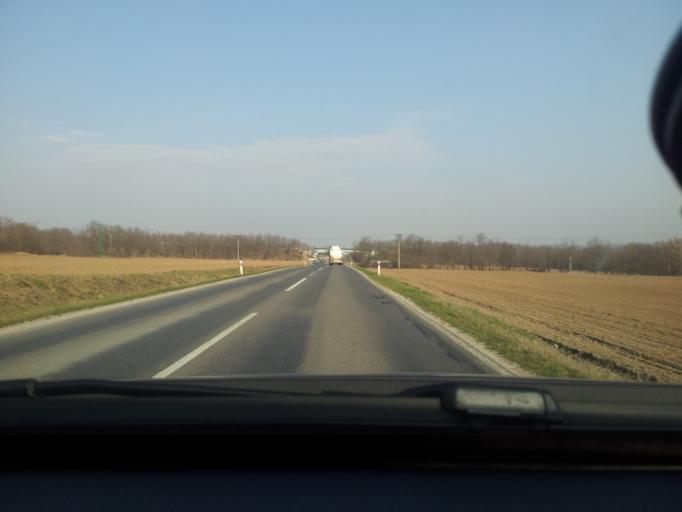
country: SK
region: Trnavsky
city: Hlohovec
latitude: 48.3791
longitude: 17.8752
